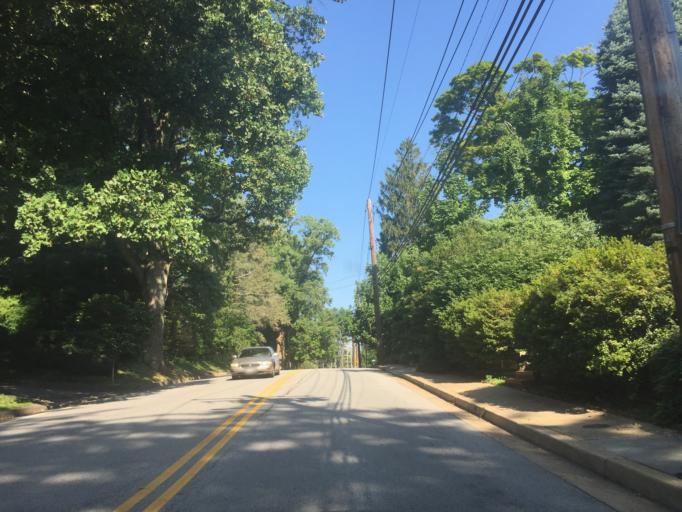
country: US
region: Maryland
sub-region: Baltimore County
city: Towson
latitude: 39.3697
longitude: -76.6347
